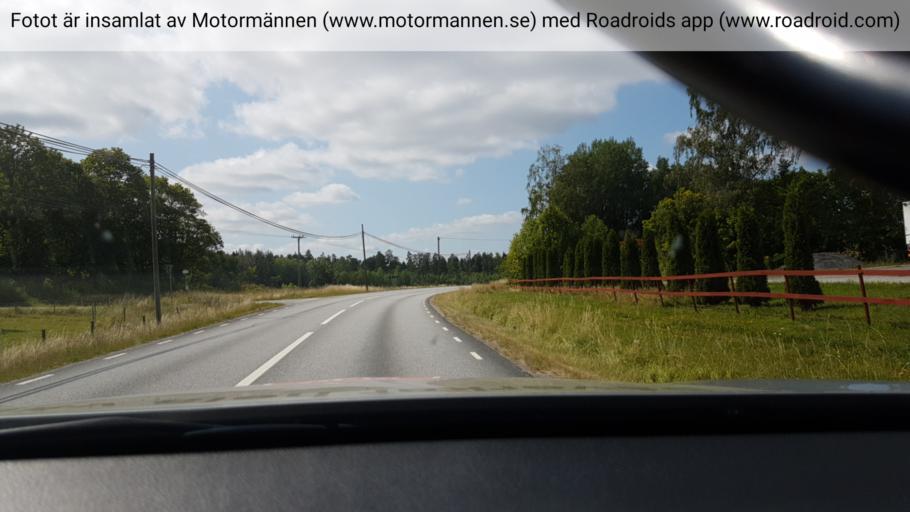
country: SE
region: Stockholm
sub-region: Vallentuna Kommun
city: Vallentuna
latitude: 59.5454
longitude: 18.1968
